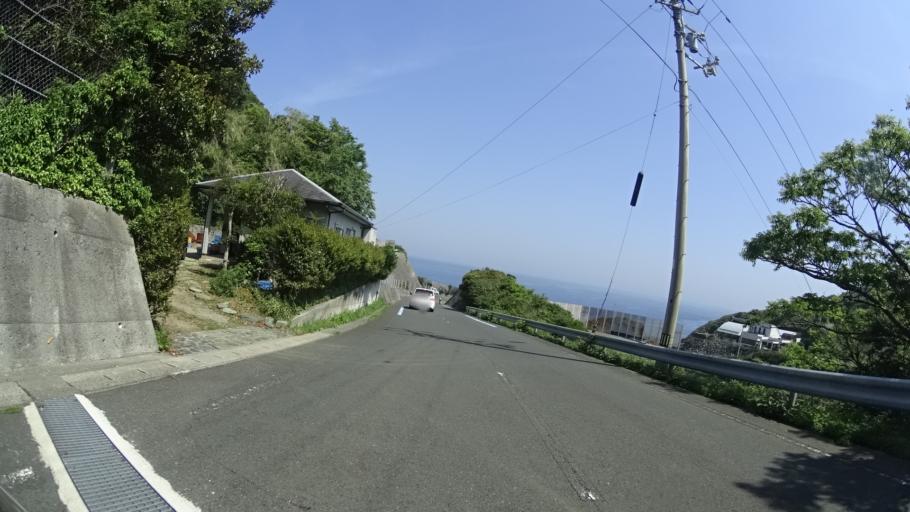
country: JP
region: Ehime
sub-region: Nishiuwa-gun
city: Ikata-cho
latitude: 33.3661
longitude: 132.0441
